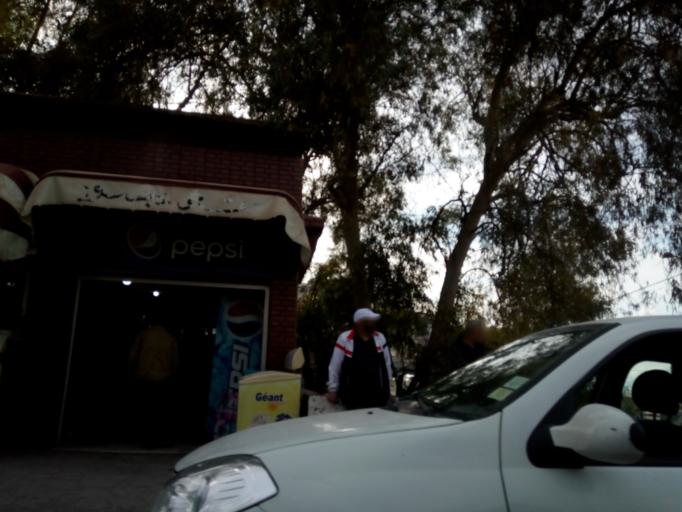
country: DZ
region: Constantine
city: Constantine
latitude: 36.3689
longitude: 6.6190
